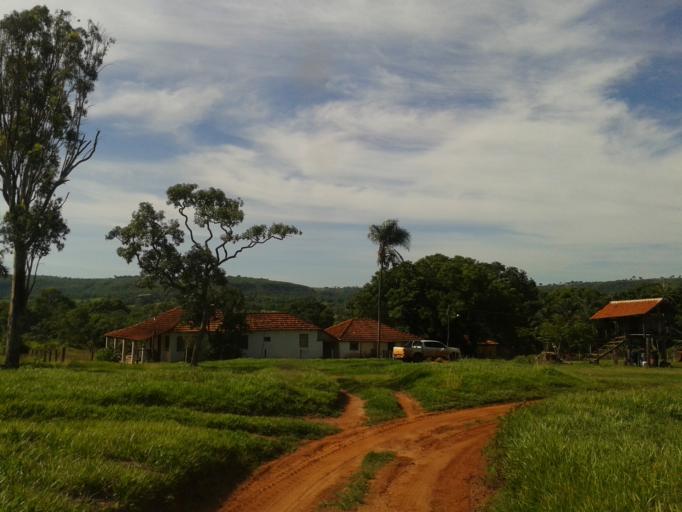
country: BR
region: Minas Gerais
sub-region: Santa Vitoria
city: Santa Vitoria
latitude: -19.0837
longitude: -50.0143
